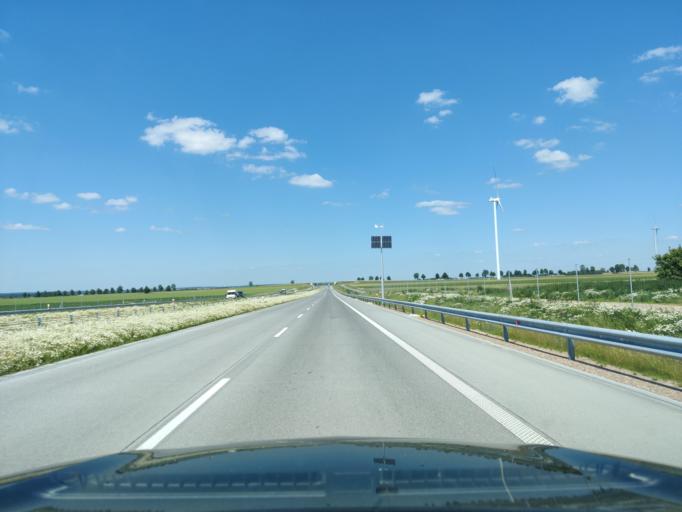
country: PL
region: Masovian Voivodeship
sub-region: Powiat mlawski
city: Wisniewo
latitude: 53.0513
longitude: 20.3618
